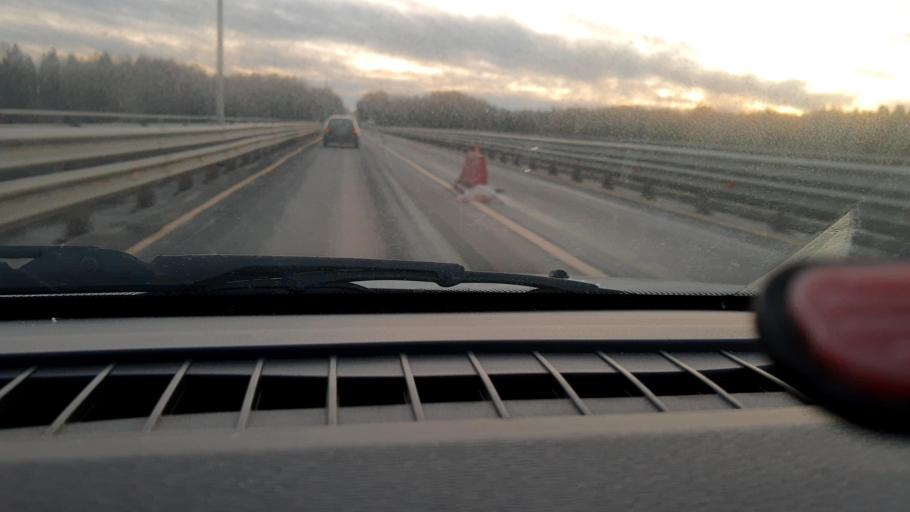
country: RU
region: Nizjnij Novgorod
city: Krasnyye Baki
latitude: 57.1095
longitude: 45.1919
